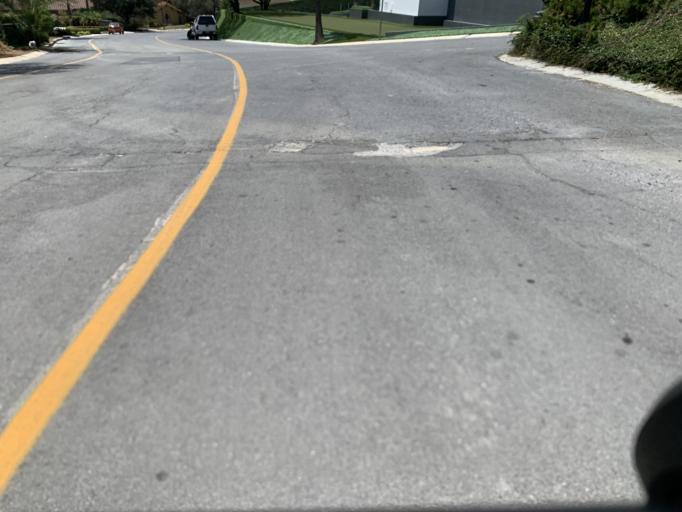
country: MX
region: Nuevo Leon
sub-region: Juarez
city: Bosques de San Pedro
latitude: 25.5195
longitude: -100.1882
